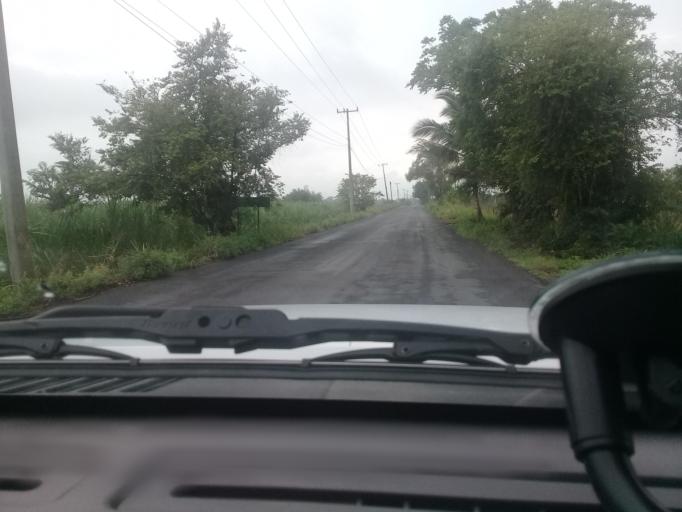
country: MX
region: Veracruz
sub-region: La Antigua
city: Nicolas Blanco (San Pancho)
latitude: 19.3562
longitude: -96.3521
